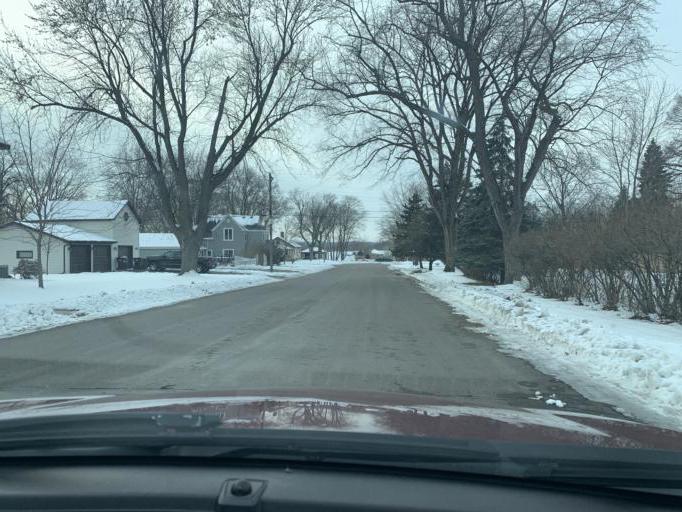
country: US
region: Minnesota
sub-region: Washington County
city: Saint Paul Park
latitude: 44.8441
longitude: -92.9900
